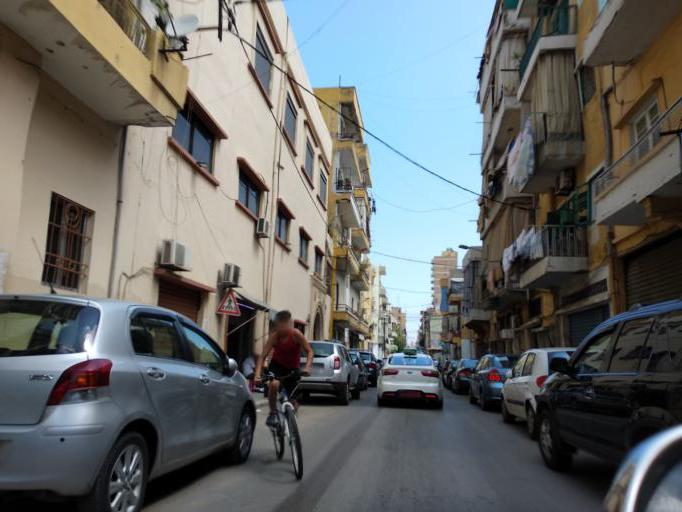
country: LB
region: Mont-Liban
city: Jdaidet el Matn
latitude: 33.8913
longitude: 35.5328
